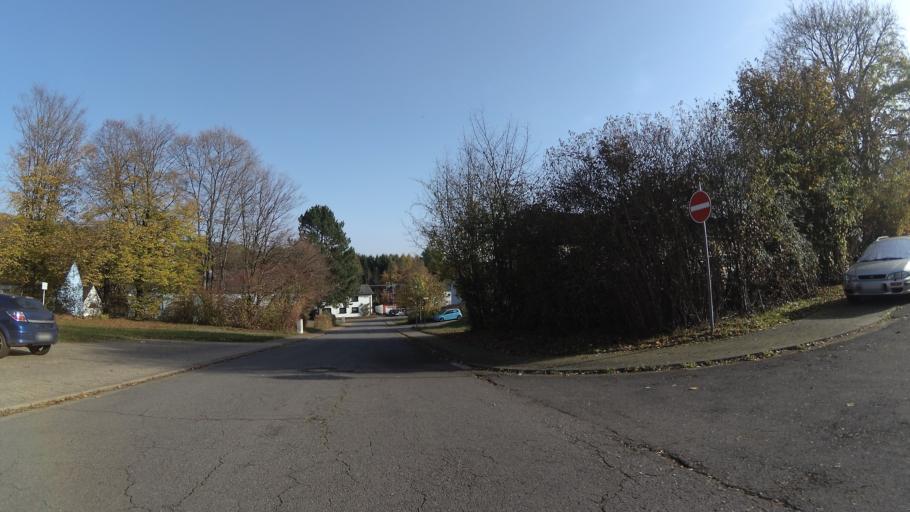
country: DE
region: Saarland
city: Bexbach
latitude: 49.3592
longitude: 7.2674
